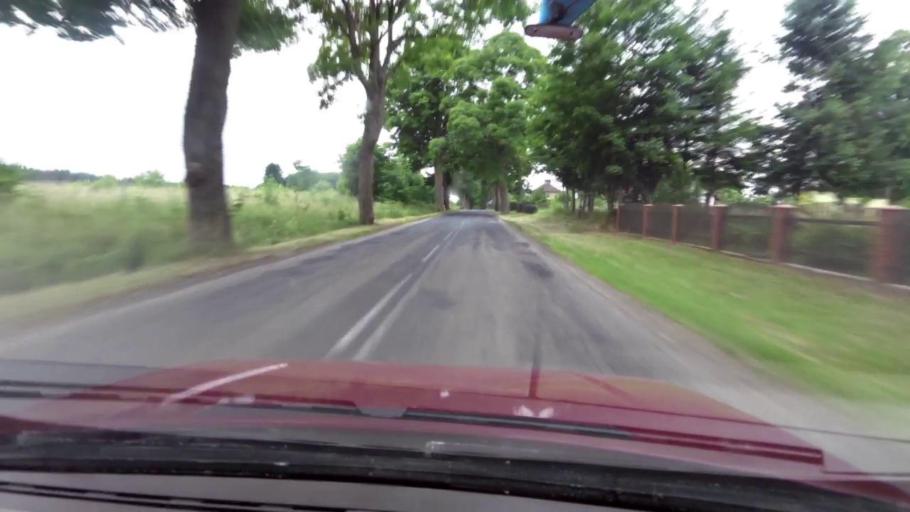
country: PL
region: West Pomeranian Voivodeship
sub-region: Powiat koszalinski
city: Sianow
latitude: 54.1743
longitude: 16.3935
